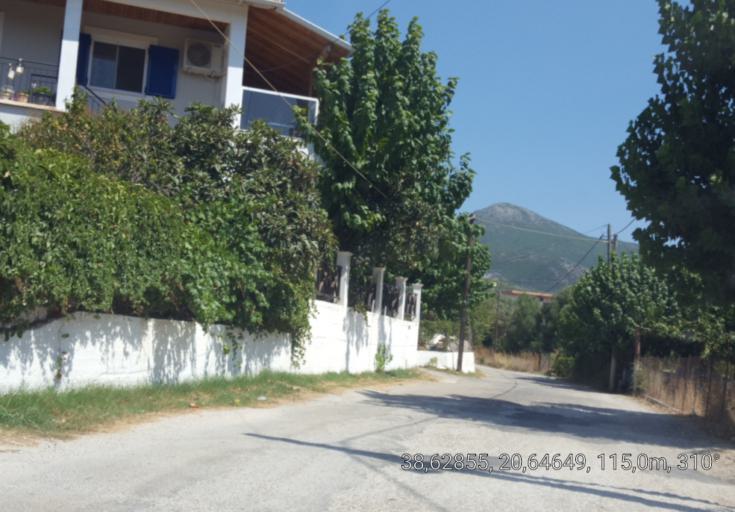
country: GR
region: Ionian Islands
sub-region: Lefkada
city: Nidri
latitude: 38.6286
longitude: 20.6464
